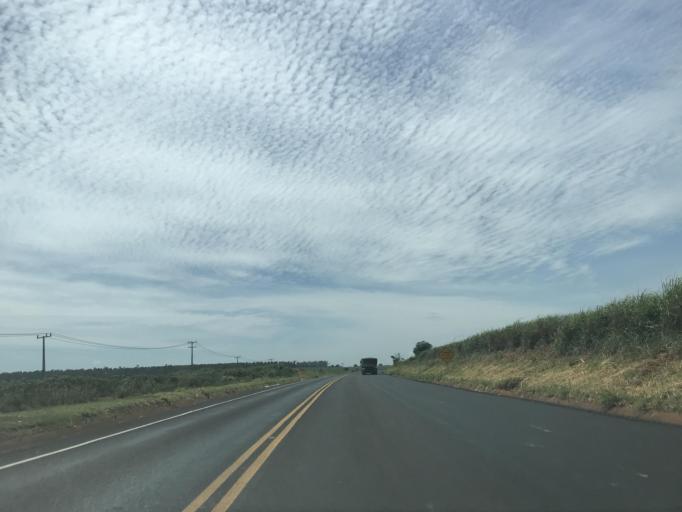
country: BR
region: Parana
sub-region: Paranavai
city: Paranavai
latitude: -23.0037
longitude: -52.5522
